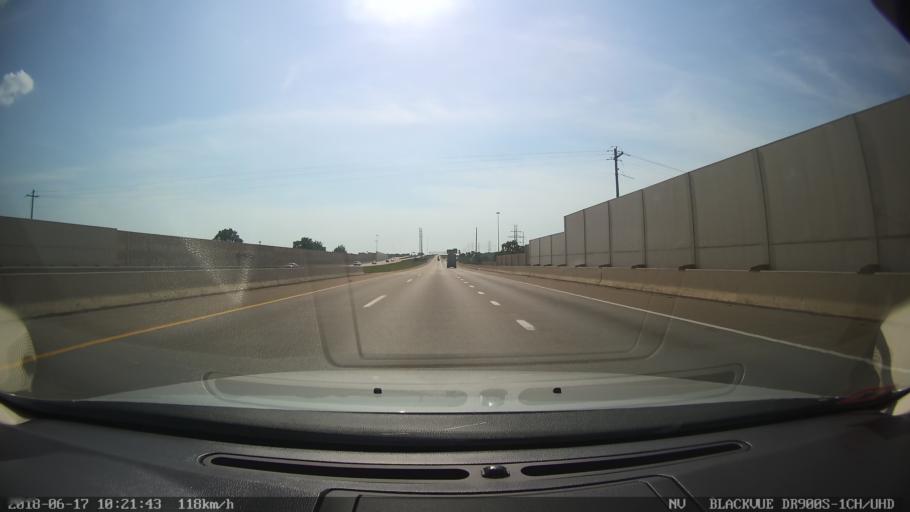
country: US
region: Michigan
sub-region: Kent County
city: Cutlerville
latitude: 42.8491
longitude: -85.6636
